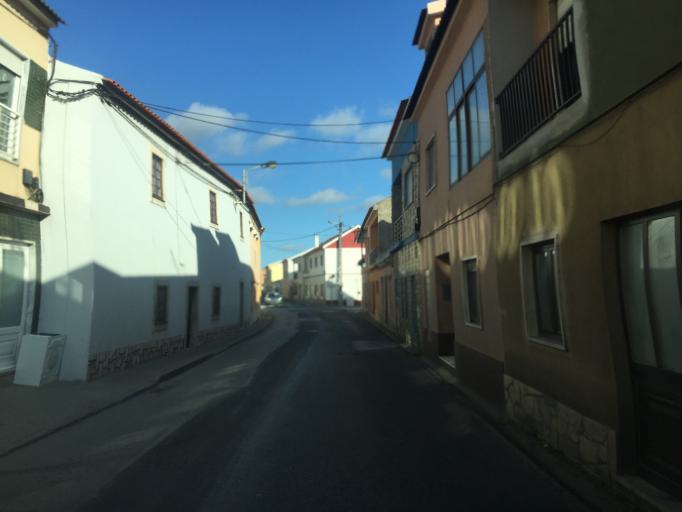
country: PT
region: Lisbon
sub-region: Torres Vedras
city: A dos Cunhados
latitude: 39.1501
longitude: -9.2969
